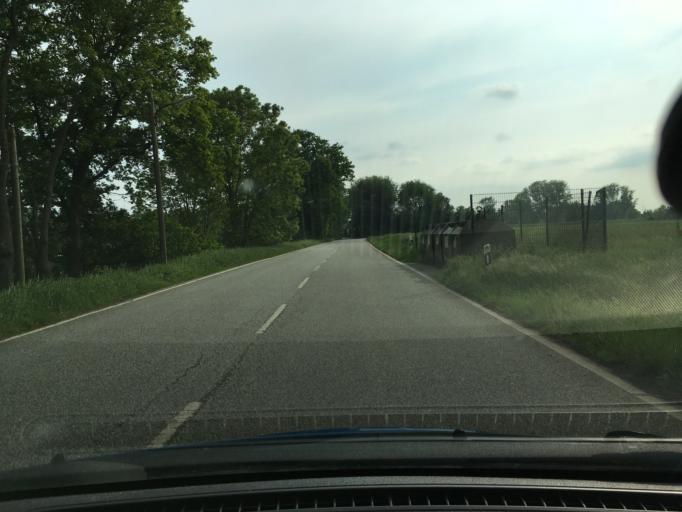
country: DE
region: Hamburg
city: Rothenburgsort
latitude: 53.4779
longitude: 10.0433
